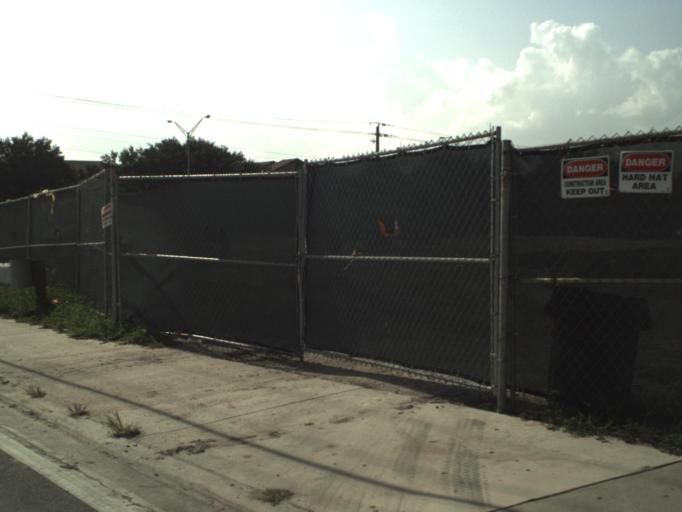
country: US
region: Florida
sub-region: Broward County
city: Coral Springs
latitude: 26.2727
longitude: -80.2654
